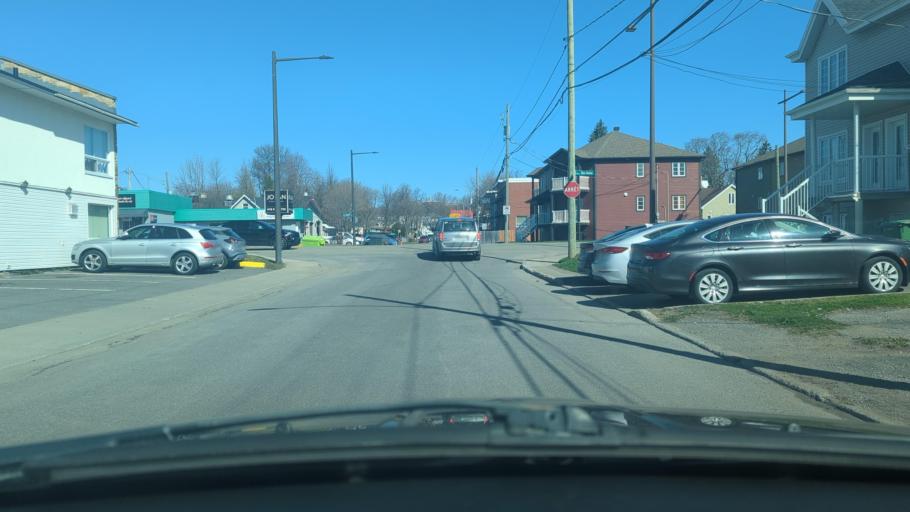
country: CA
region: Quebec
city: Quebec
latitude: 46.8481
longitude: -71.2081
